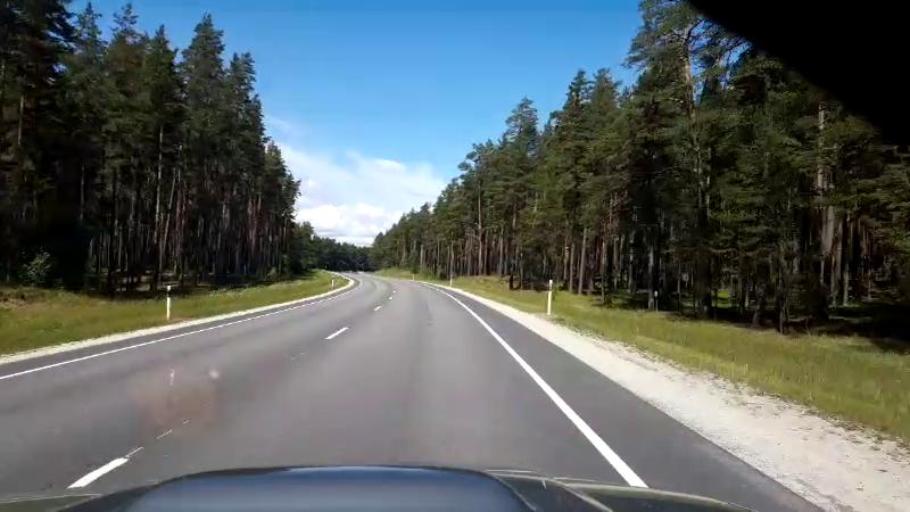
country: EE
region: Paernumaa
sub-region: Paernu linn
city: Parnu
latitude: 58.1464
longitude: 24.5032
